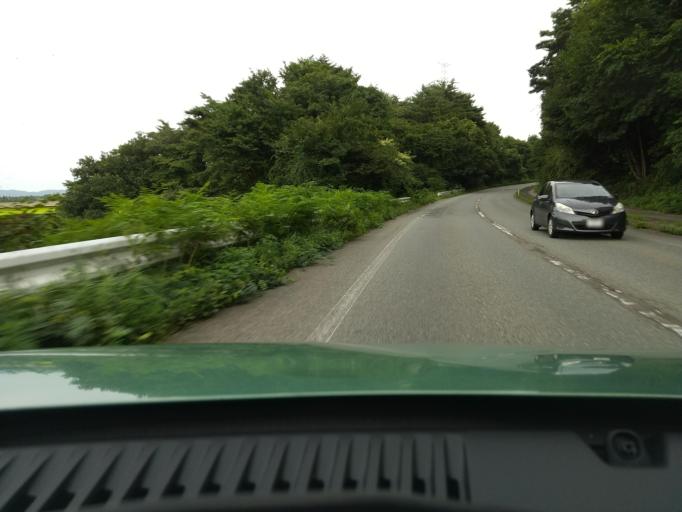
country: JP
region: Akita
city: Akita Shi
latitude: 39.8140
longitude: 140.0894
